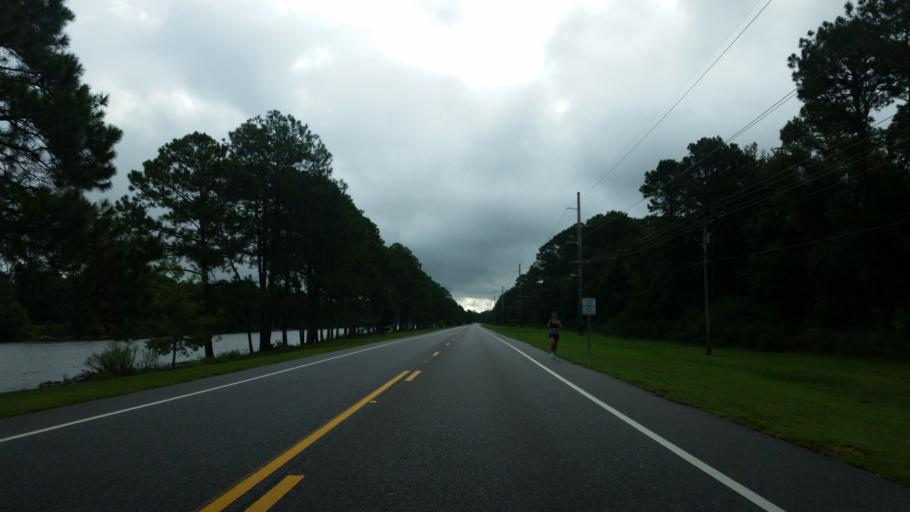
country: US
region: Alabama
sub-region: Baldwin County
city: Gulf Shores
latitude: 30.2794
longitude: -87.6635
